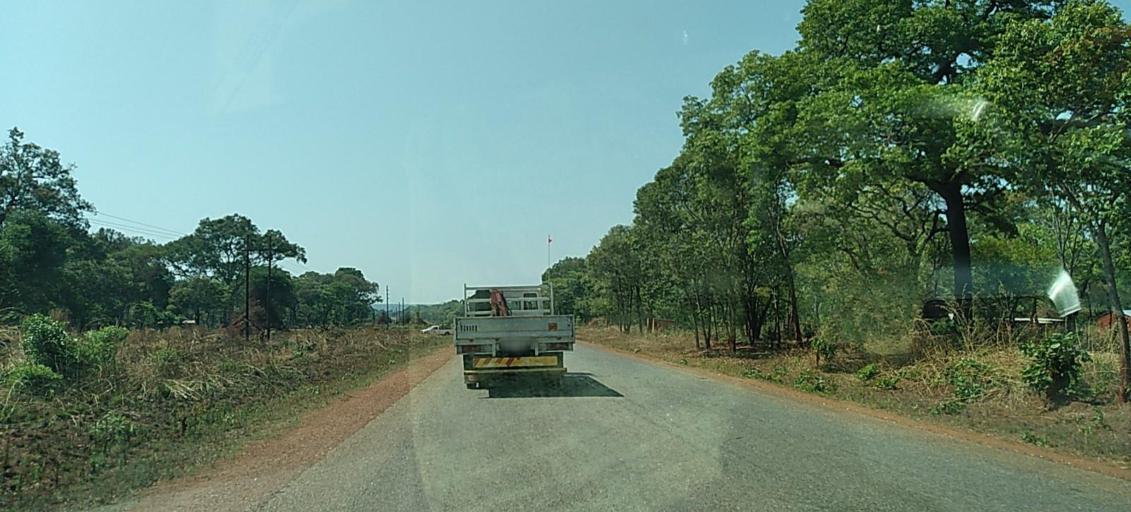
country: ZM
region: North-Western
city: Solwezi
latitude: -12.2087
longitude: 25.5582
